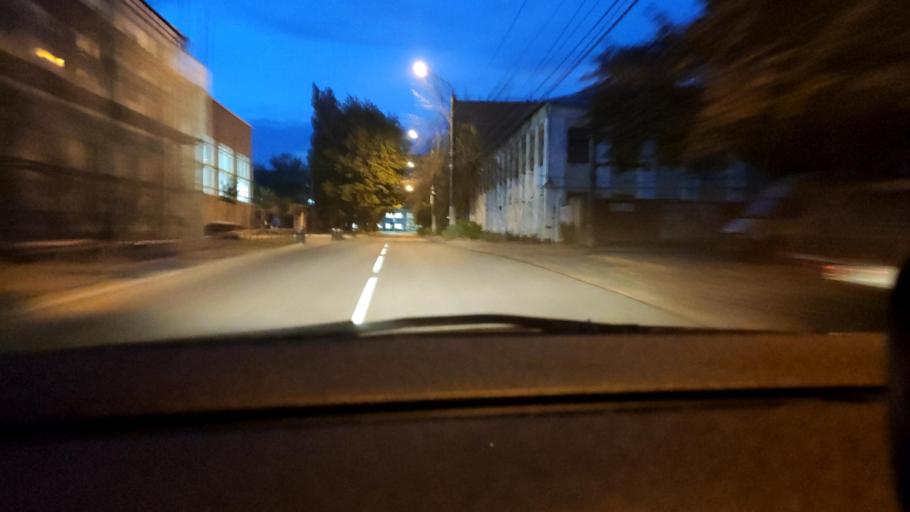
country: RU
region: Voronezj
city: Voronezh
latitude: 51.6858
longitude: 39.1700
